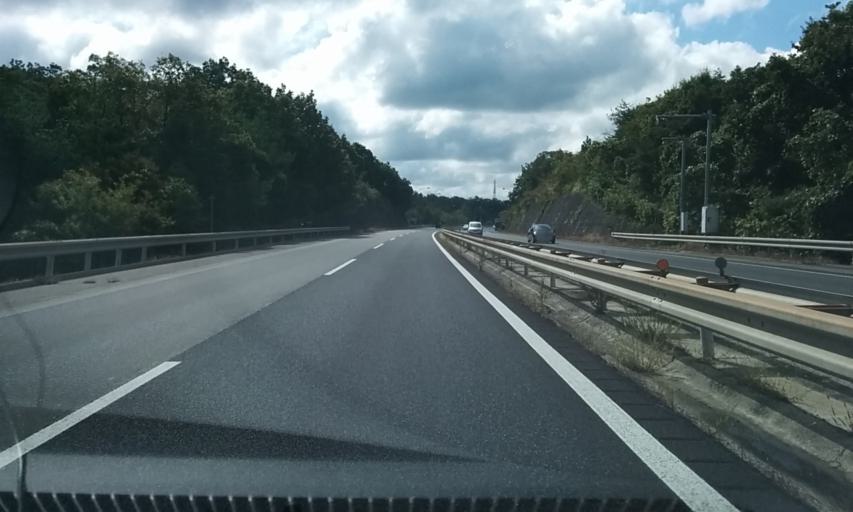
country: JP
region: Hyogo
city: Sandacho
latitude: 34.9104
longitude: 135.1553
